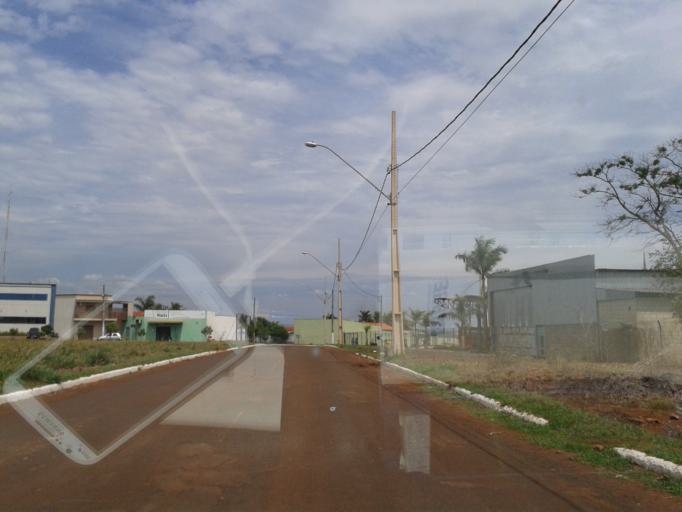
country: BR
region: Goias
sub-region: Itumbiara
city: Itumbiara
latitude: -18.4291
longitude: -49.1914
